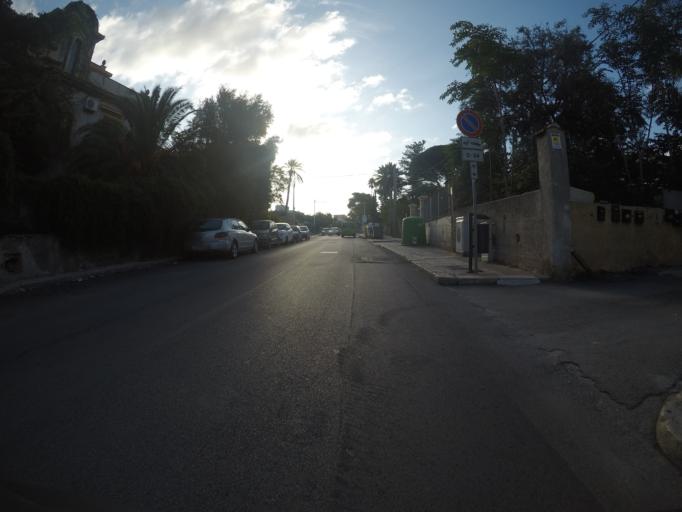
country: IT
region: Sicily
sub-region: Palermo
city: Isola delle Femmine
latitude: 38.1963
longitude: 13.2789
